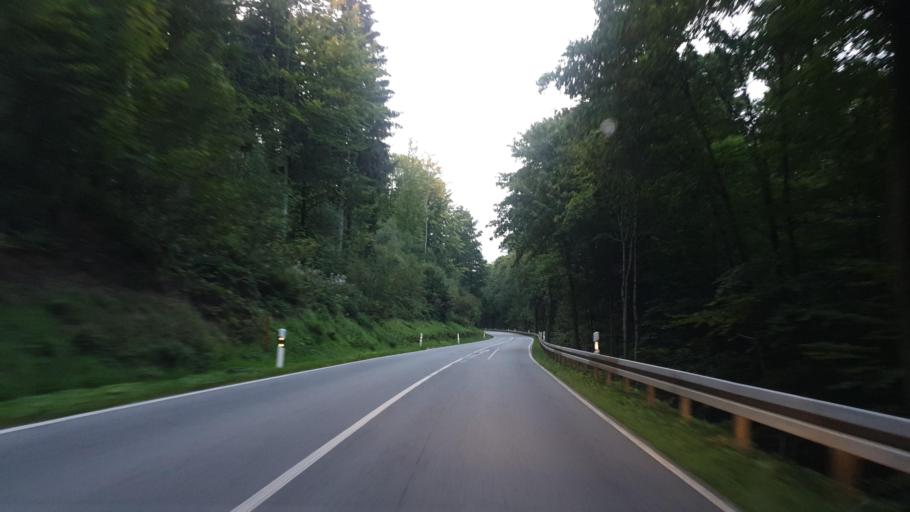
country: DE
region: Saxony
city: Sosa
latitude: 50.4717
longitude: 12.6285
